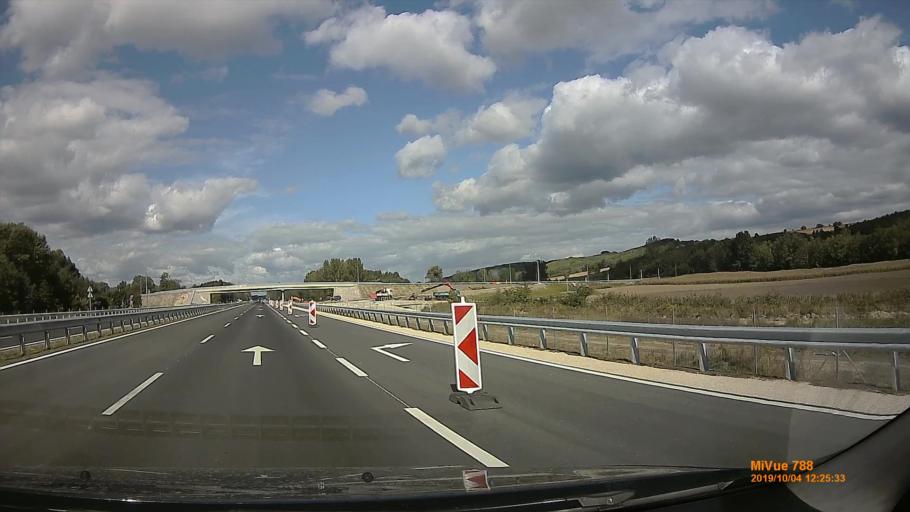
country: HU
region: Somogy
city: Karad
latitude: 46.6648
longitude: 17.7835
